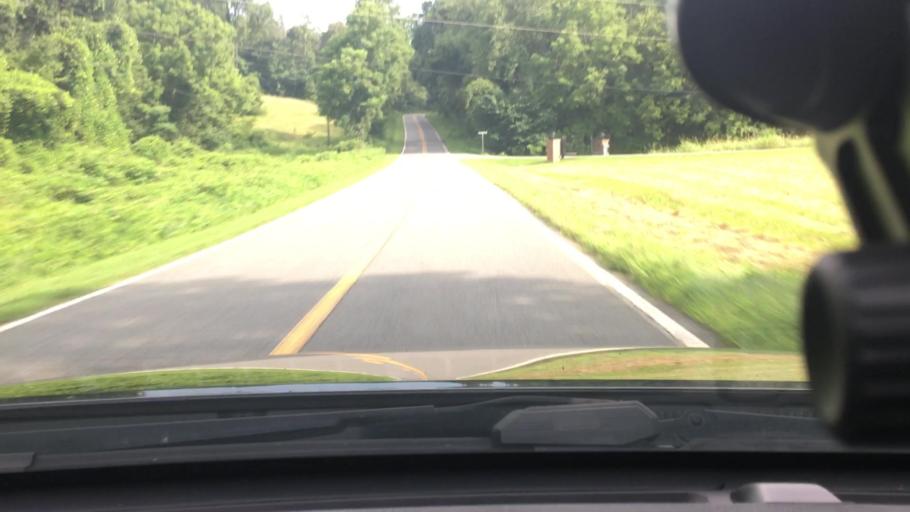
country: US
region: North Carolina
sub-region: Rutherford County
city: Rutherfordton
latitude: 35.3944
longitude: -81.9712
